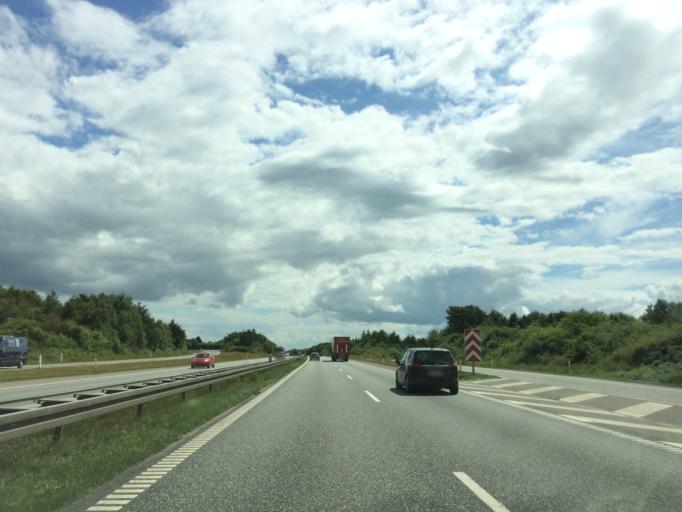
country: DK
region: North Denmark
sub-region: Mariagerfjord Kommune
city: Hobro
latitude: 56.7366
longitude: 9.7025
